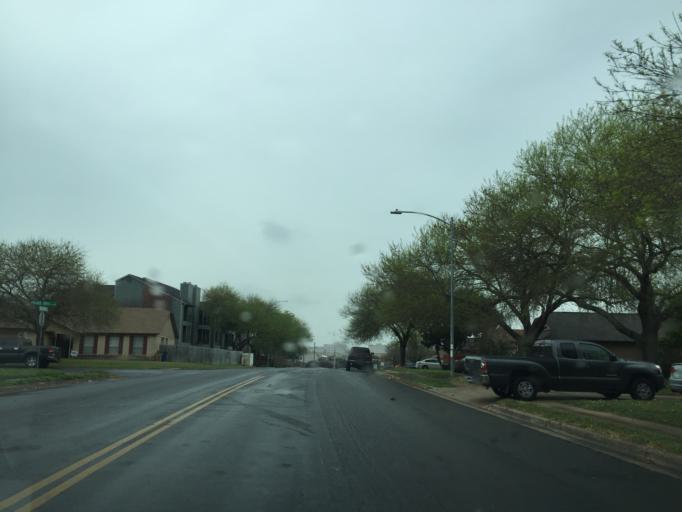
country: US
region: Texas
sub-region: Travis County
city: Wells Branch
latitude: 30.3978
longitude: -97.7025
